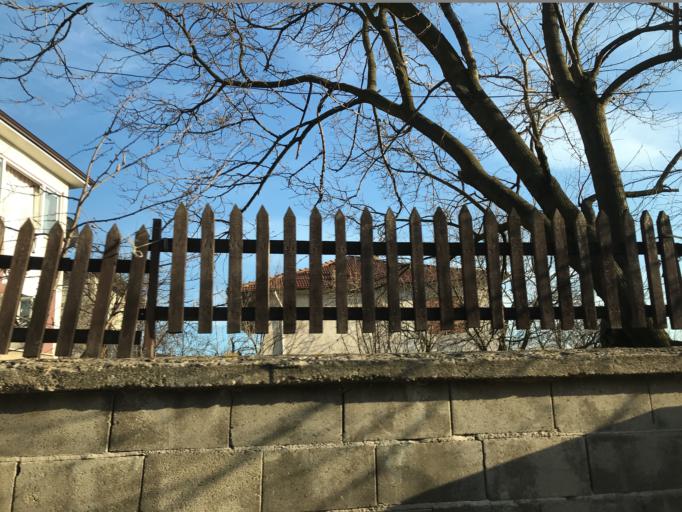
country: TR
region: Karabuk
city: Safranbolu
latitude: 41.2589
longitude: 32.6826
